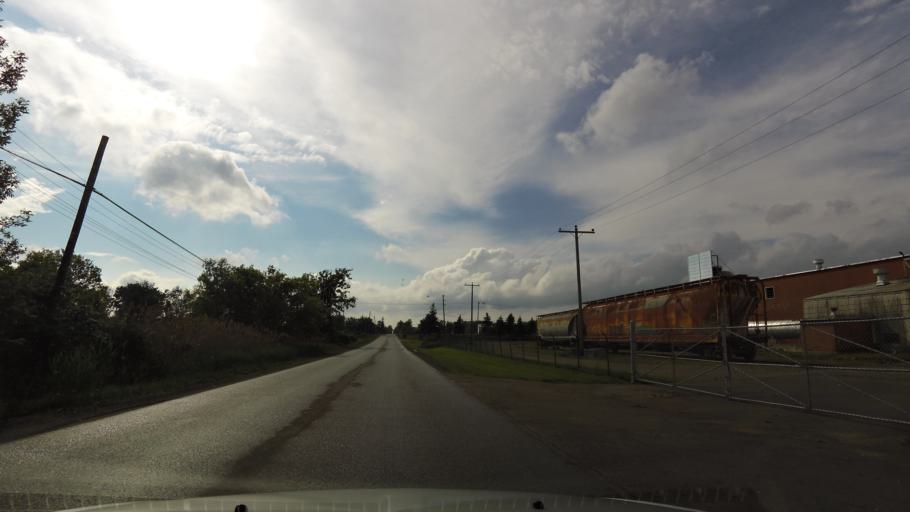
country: CA
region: Ontario
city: Ancaster
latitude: 43.0116
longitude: -80.0189
